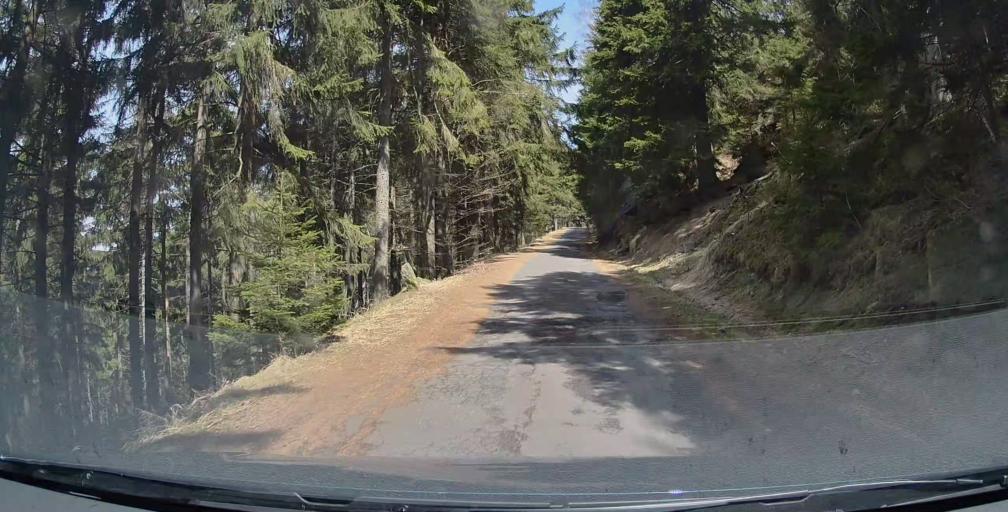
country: CZ
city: Machov
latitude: 50.4726
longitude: 16.2881
